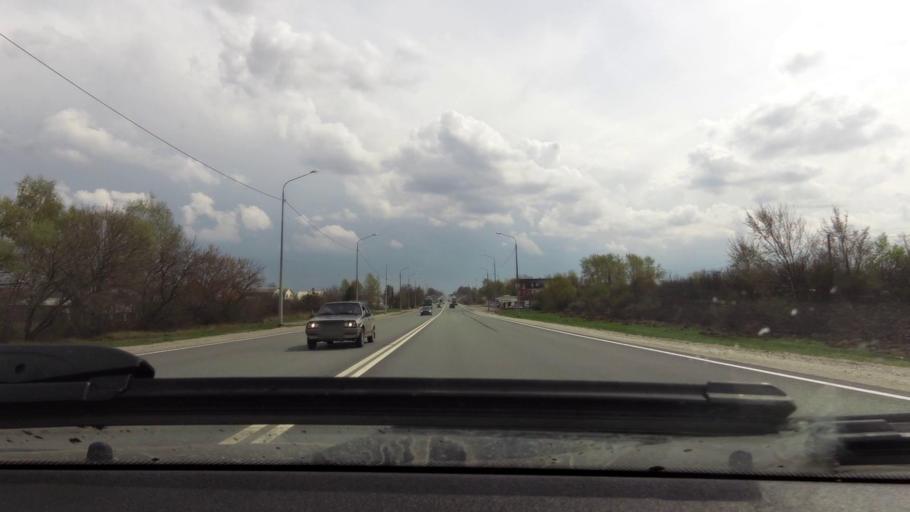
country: RU
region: Rjazan
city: Bagramovo
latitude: 54.7334
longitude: 39.4578
